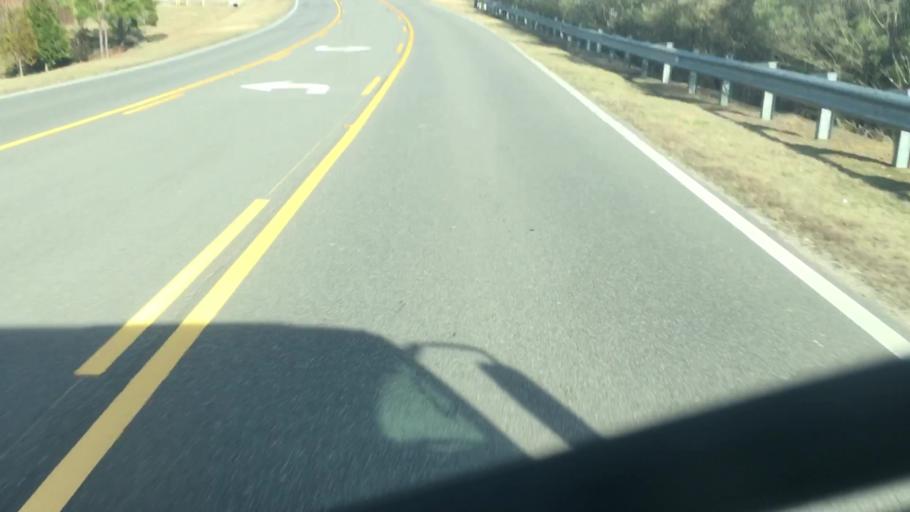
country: US
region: Alabama
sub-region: Shelby County
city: Brook Highland
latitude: 33.4700
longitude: -86.6763
